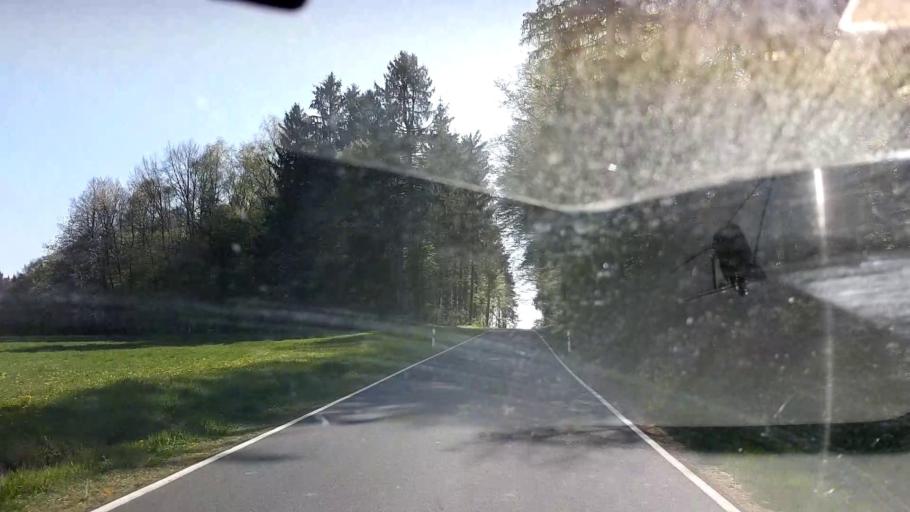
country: DE
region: Bavaria
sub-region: Upper Franconia
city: Pottenstein
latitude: 49.7968
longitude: 11.3986
